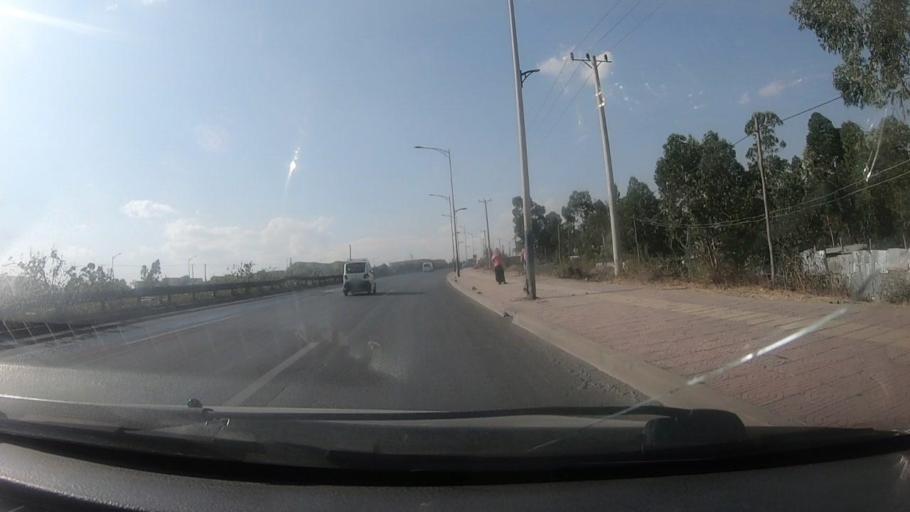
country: ET
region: Adis Abeba
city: Addis Ababa
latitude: 8.9063
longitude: 38.7424
